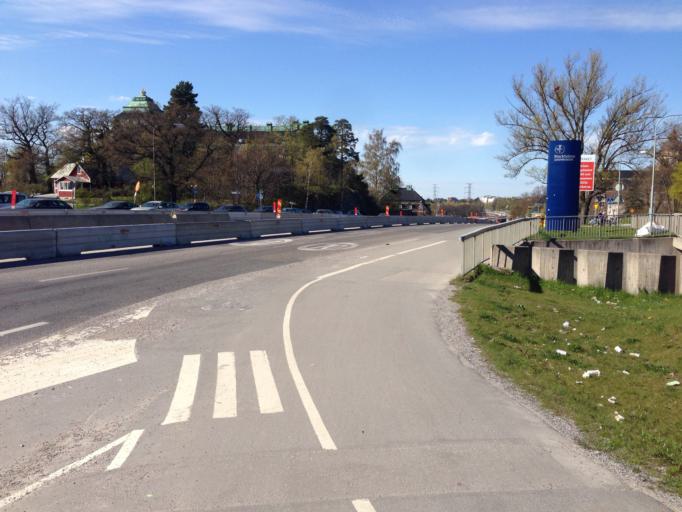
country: SE
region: Stockholm
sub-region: Norrtalje Kommun
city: Bergshamra
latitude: 59.3651
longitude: 18.0538
